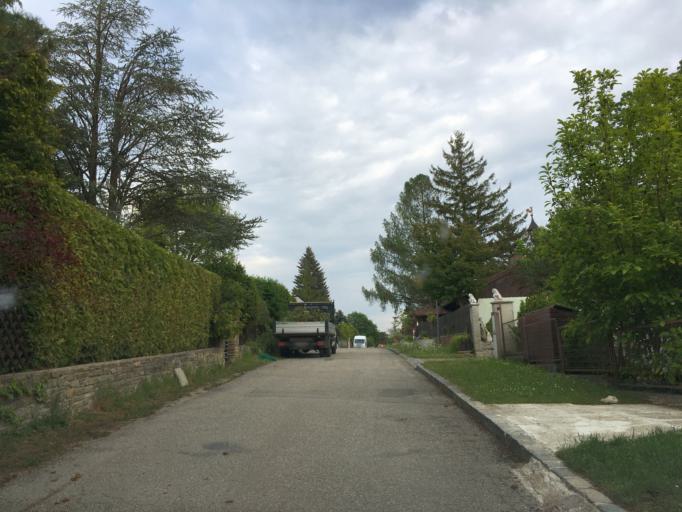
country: AT
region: Lower Austria
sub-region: Politischer Bezirk Sankt Polten
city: Maria-Anzbach
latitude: 48.1917
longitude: 15.9367
